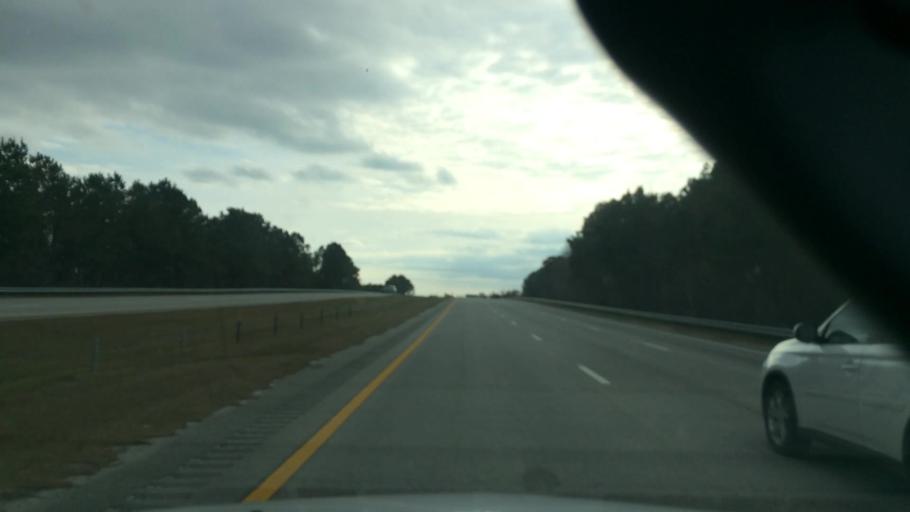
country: US
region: South Carolina
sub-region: Horry County
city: North Myrtle Beach
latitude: 33.8553
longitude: -78.6974
